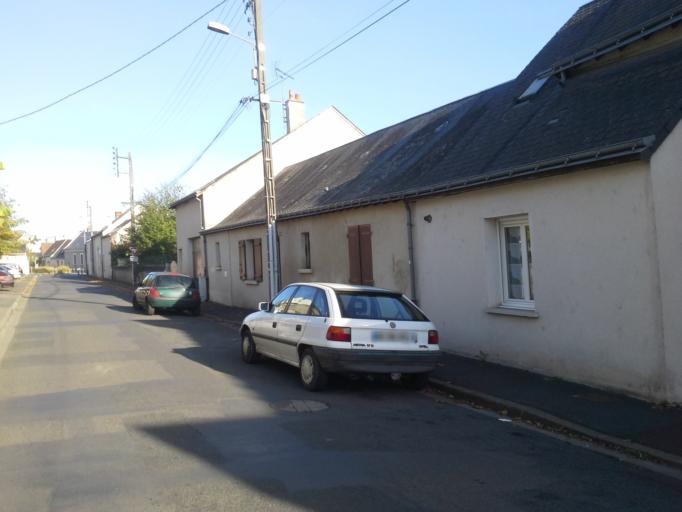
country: FR
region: Centre
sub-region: Departement d'Indre-et-Loire
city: La Riche
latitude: 47.3872
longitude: 0.6607
